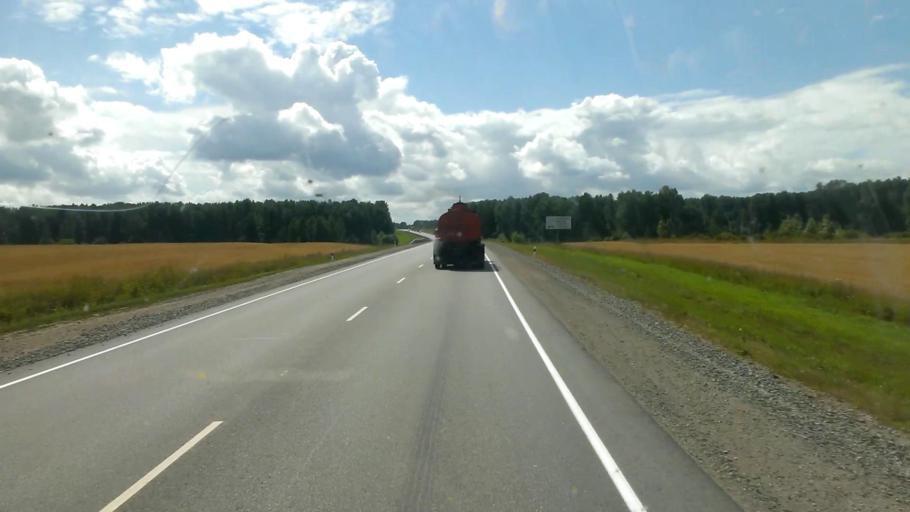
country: RU
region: Altai Krai
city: Troitskoye
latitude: 52.9863
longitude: 84.7436
